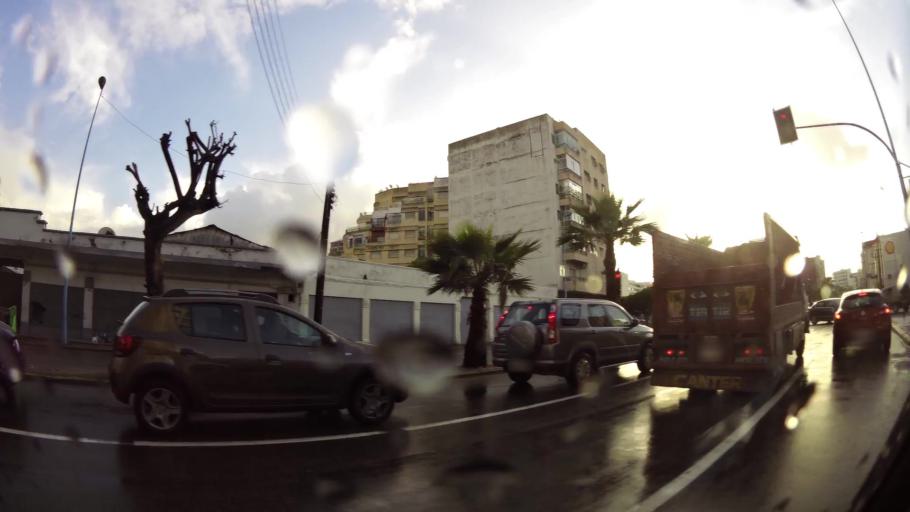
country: MA
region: Grand Casablanca
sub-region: Casablanca
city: Casablanca
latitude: 33.5880
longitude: -7.5994
